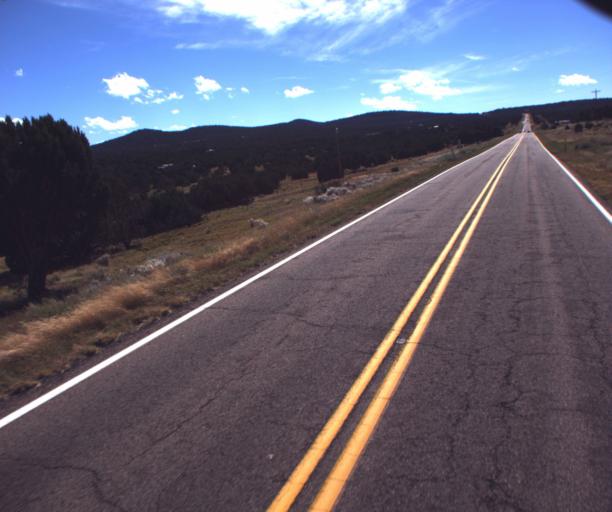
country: US
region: Arizona
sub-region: Navajo County
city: White Mountain Lake
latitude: 34.3303
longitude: -109.7465
